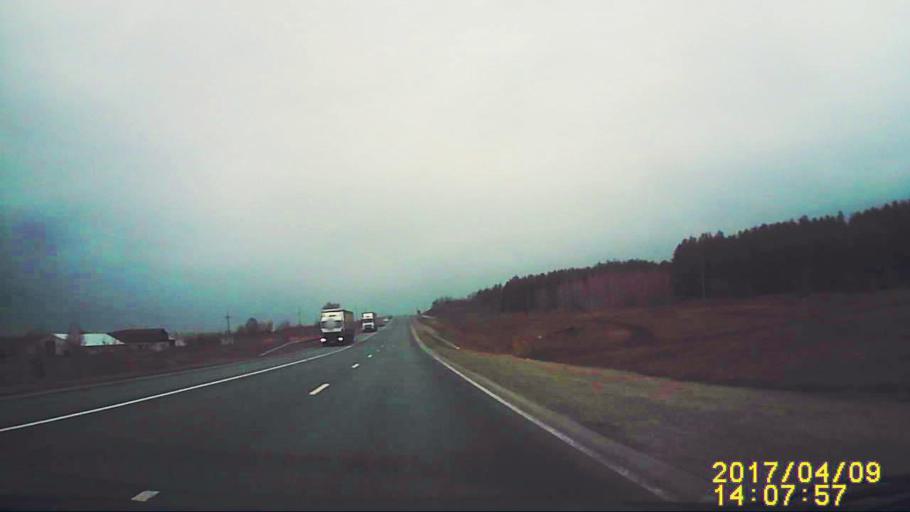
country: RU
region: Ulyanovsk
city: Silikatnyy
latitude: 54.0161
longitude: 48.2167
